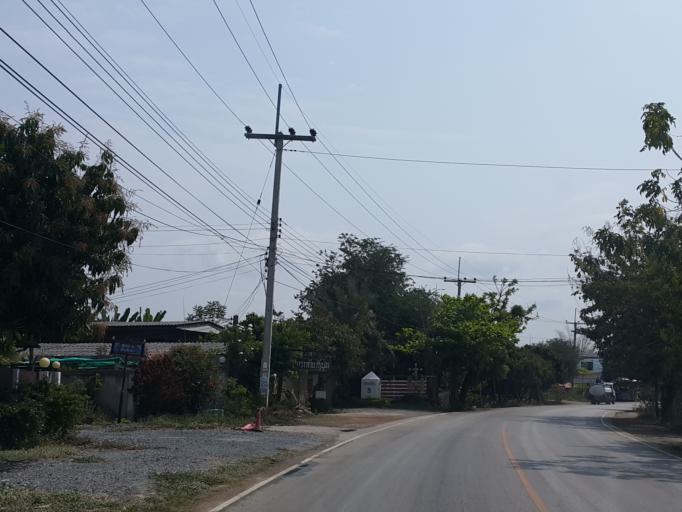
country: TH
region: Lamphun
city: Ban Thi
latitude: 18.6595
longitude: 99.1100
